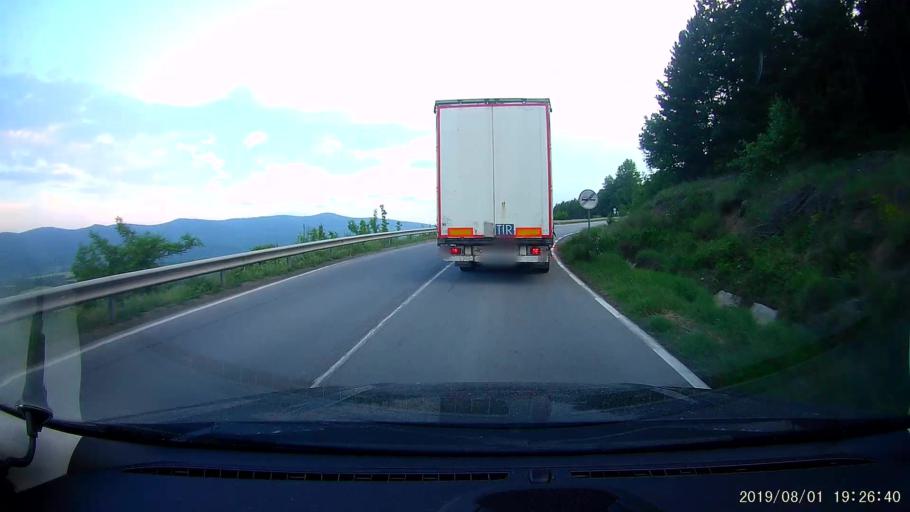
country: BG
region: Burgas
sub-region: Obshtina Sungurlare
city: Sungurlare
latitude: 42.8554
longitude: 26.9393
